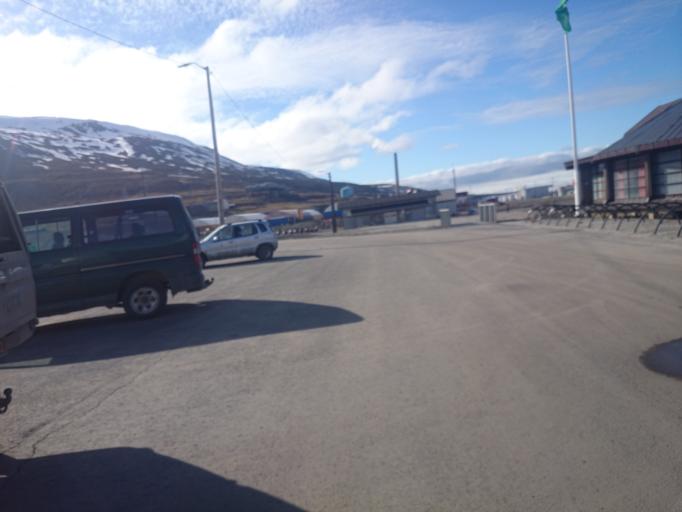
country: SJ
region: Svalbard
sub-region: Spitsbergen
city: Longyearbyen
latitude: 78.2224
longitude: 15.6492
